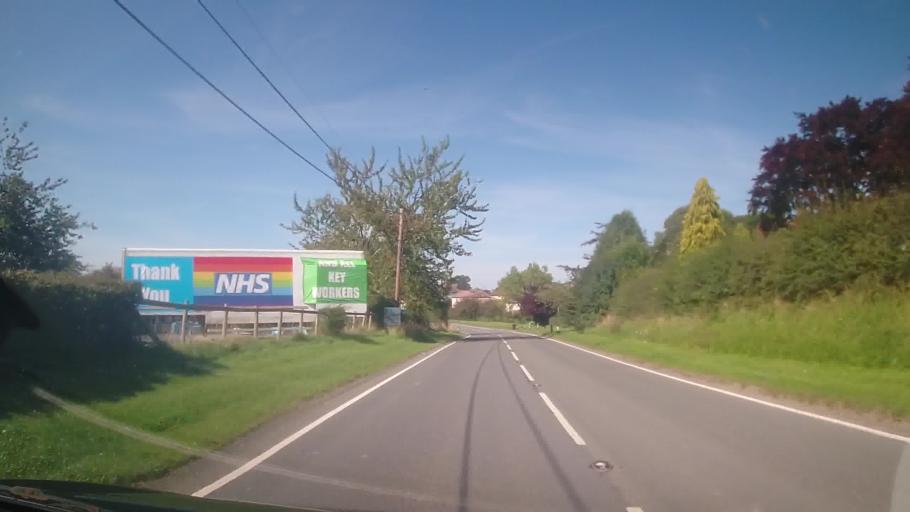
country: GB
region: England
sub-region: Shropshire
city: Mainstone
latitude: 52.5356
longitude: -3.0609
